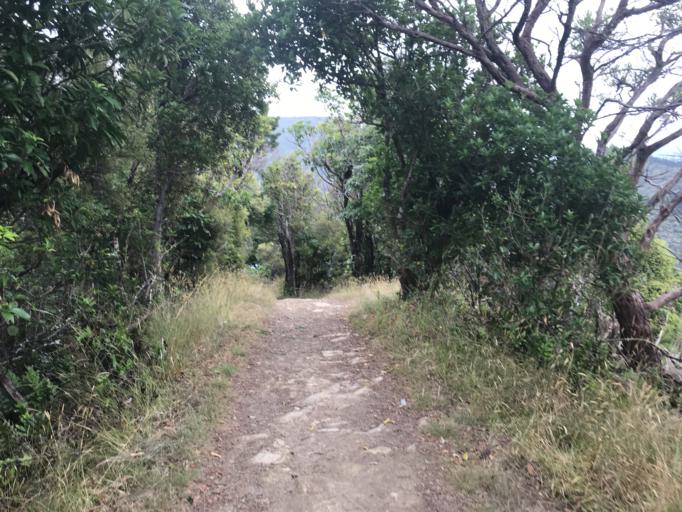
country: NZ
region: Marlborough
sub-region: Marlborough District
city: Picton
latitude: -41.2181
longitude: 173.9762
